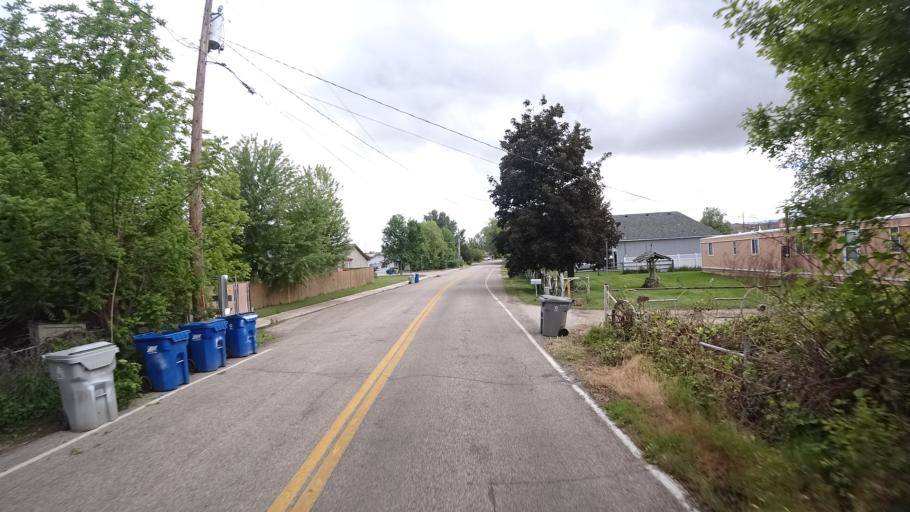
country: US
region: Idaho
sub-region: Ada County
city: Eagle
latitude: 43.6752
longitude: -116.2991
